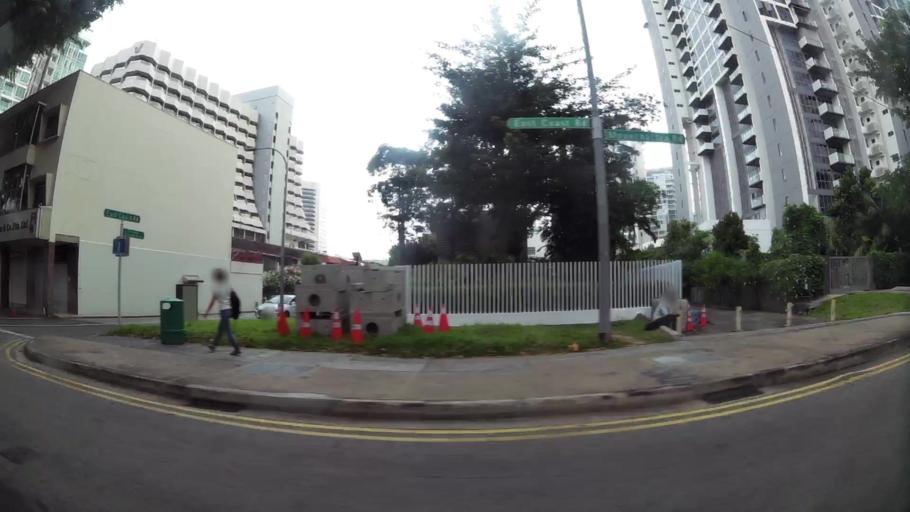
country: SG
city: Singapore
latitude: 1.3040
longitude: 103.9021
